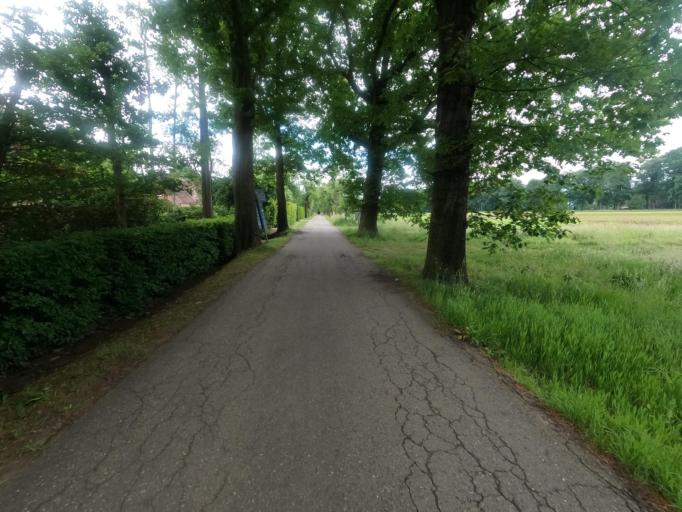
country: BE
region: Flanders
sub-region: Provincie Antwerpen
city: Heist-op-den-Berg
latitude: 51.0653
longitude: 4.6865
